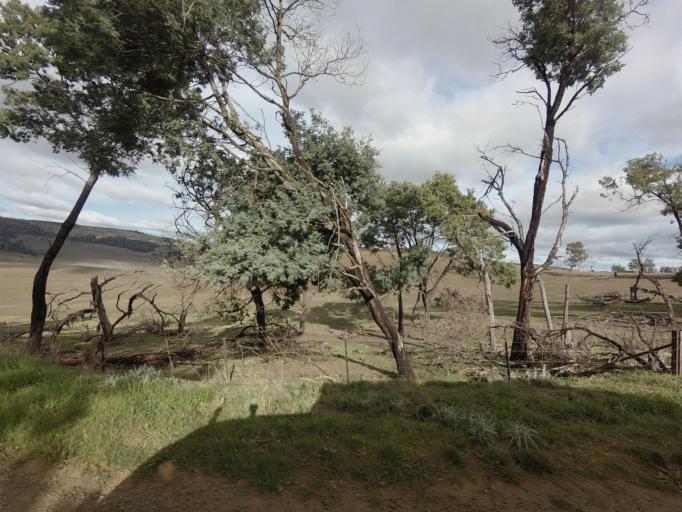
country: AU
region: Tasmania
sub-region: Brighton
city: Bridgewater
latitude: -42.4610
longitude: 147.2680
